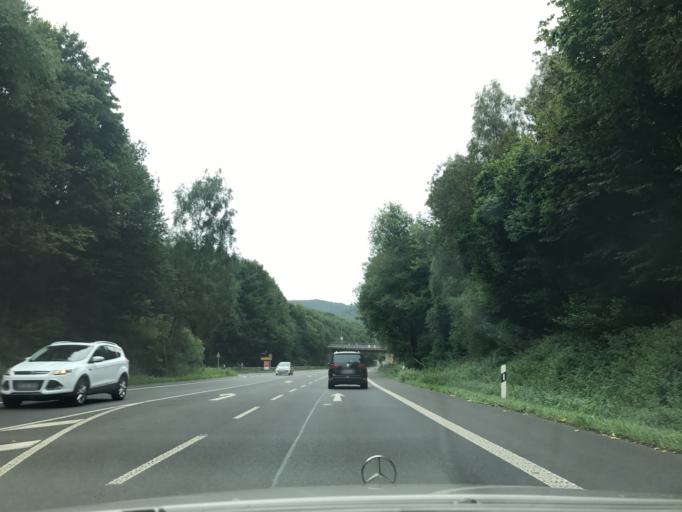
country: DE
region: North Rhine-Westphalia
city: Gevelsberg
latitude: 51.3381
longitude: 7.3560
